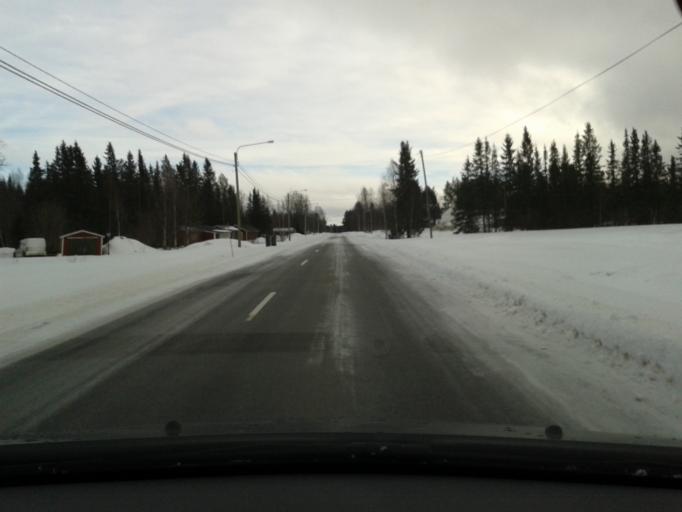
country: SE
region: Vaesterbotten
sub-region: Vilhelmina Kommun
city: Sjoberg
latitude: 64.6504
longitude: 16.3334
